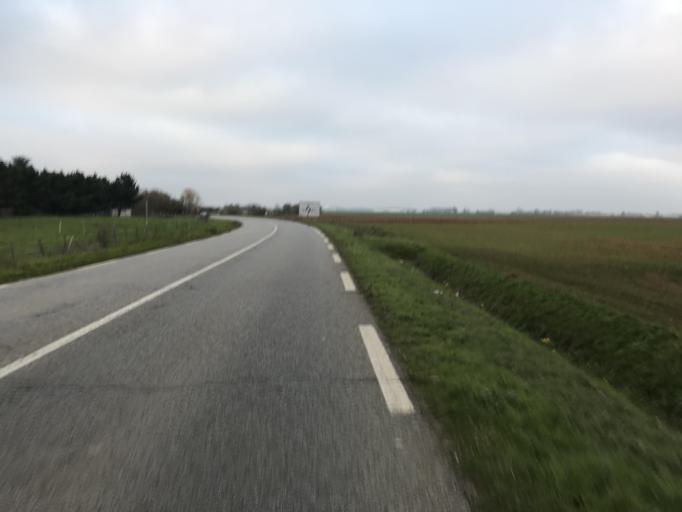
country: FR
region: Ile-de-France
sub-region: Departement des Yvelines
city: Chateaufort
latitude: 48.7373
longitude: 2.0973
